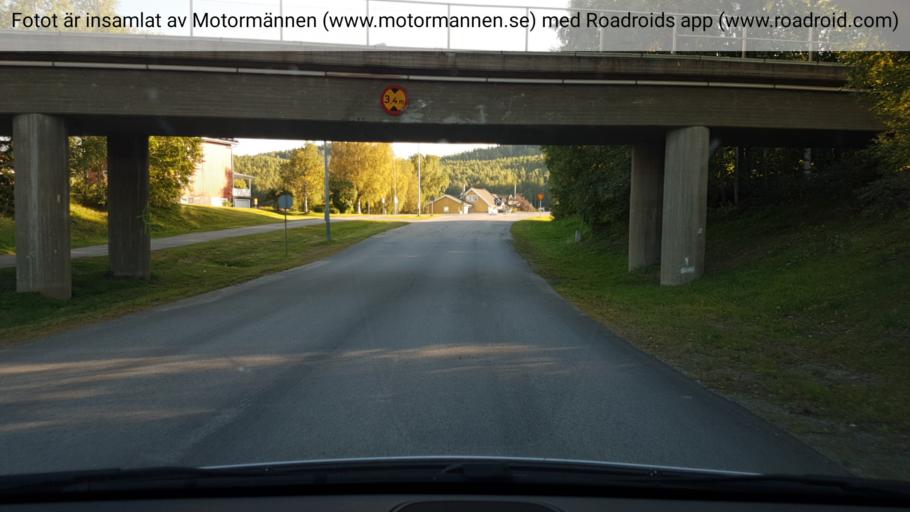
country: SE
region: Vaesterbotten
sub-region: Vannas Kommun
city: Vannasby
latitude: 63.9152
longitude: 19.8127
